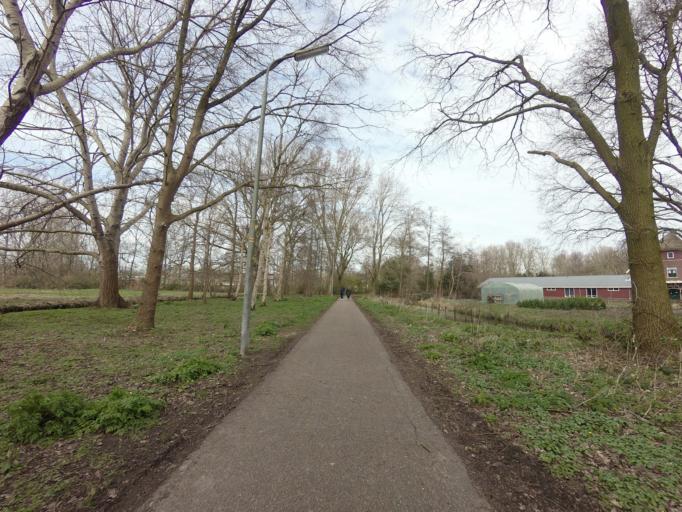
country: NL
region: North Holland
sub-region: Gemeente Uithoorn
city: Uithoorn
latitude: 52.2428
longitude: 4.8373
